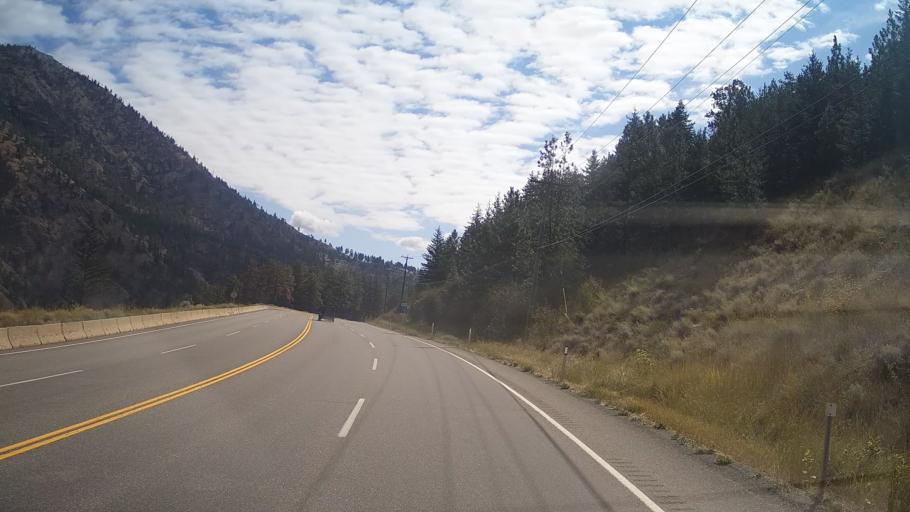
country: CA
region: British Columbia
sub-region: Thompson-Nicola Regional District
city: Ashcroft
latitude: 50.2541
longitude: -121.5154
